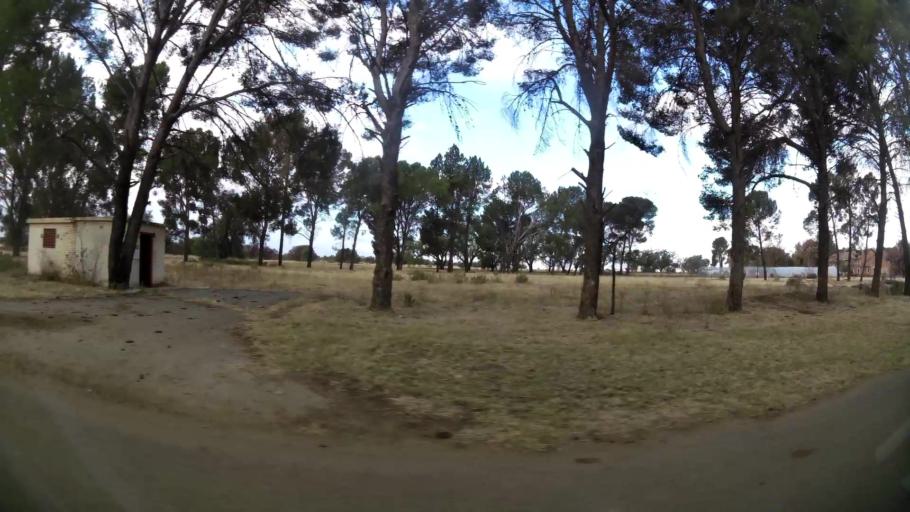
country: ZA
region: Orange Free State
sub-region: Lejweleputswa District Municipality
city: Welkom
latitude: -28.0137
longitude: 26.7157
